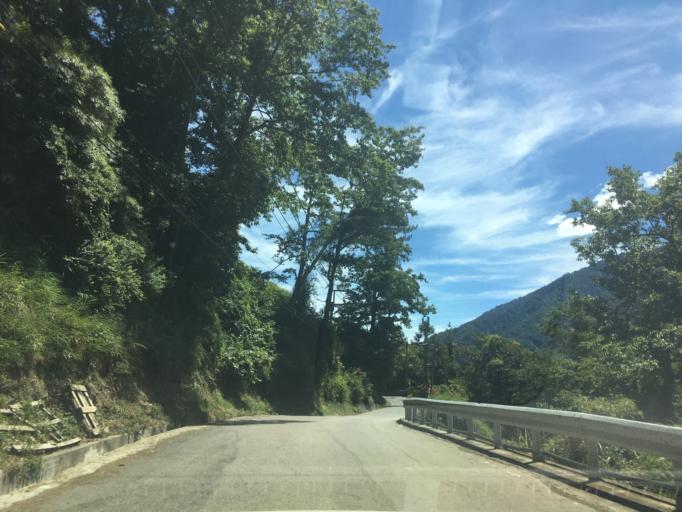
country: TW
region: Taiwan
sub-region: Nantou
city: Puli
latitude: 24.2341
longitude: 121.2546
